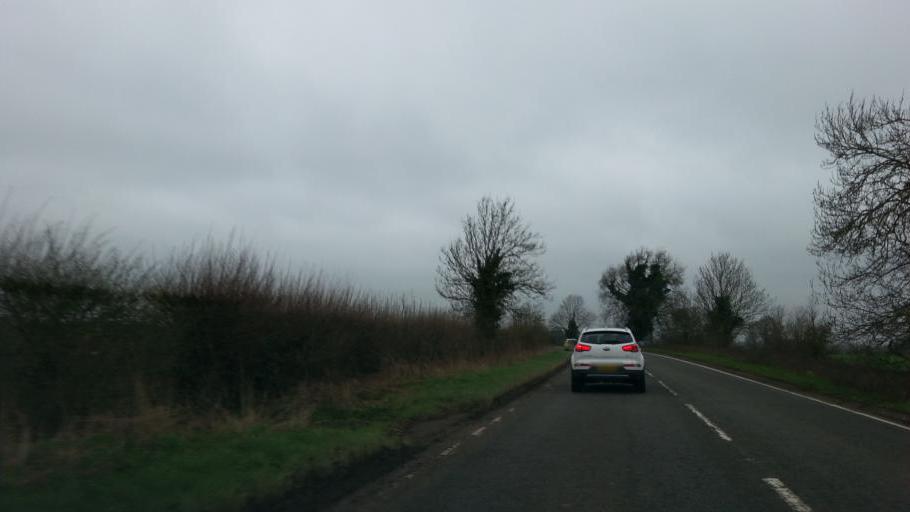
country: GB
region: England
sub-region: Oxfordshire
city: Adderbury
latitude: 52.0631
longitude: -1.2486
